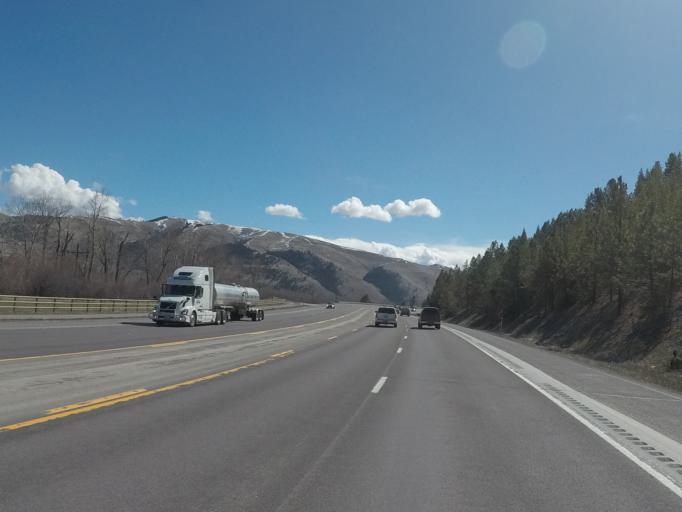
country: US
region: Montana
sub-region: Missoula County
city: Lolo
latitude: 46.7729
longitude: -114.0835
